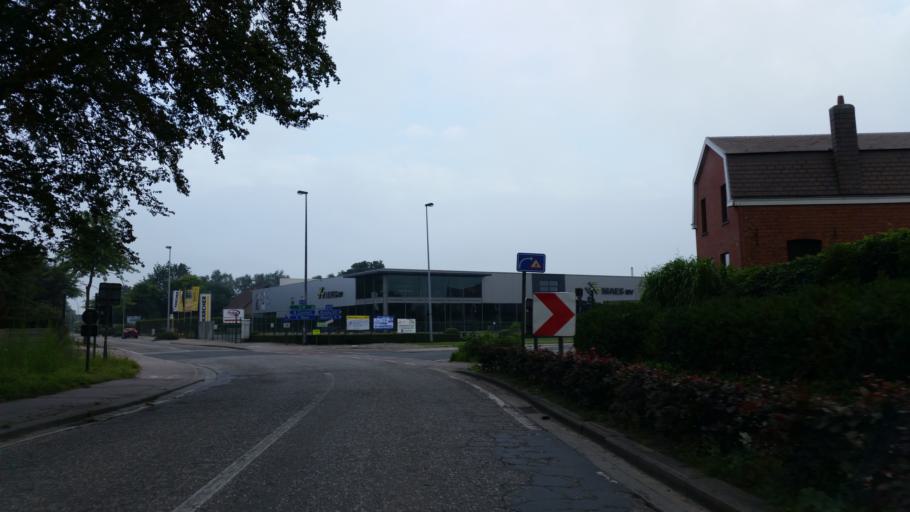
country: BE
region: Flanders
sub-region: Provincie Antwerpen
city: Hoogstraten
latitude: 51.4260
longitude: 4.7593
